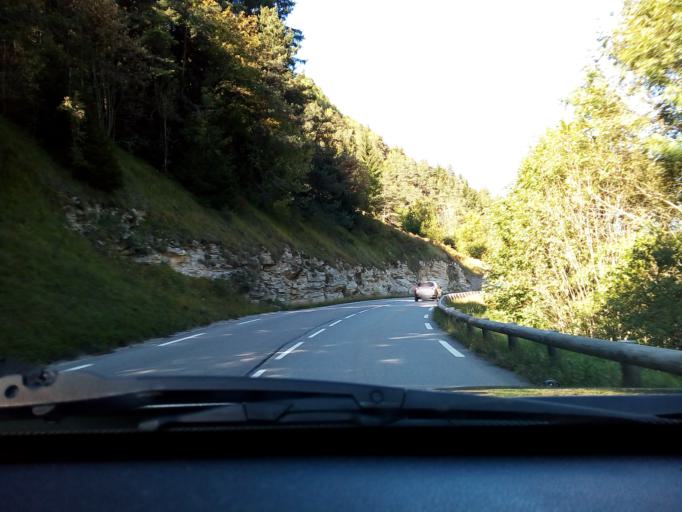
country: FR
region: Rhone-Alpes
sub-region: Departement de l'Isere
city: Lans-en-Vercors
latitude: 45.1711
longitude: 5.6138
